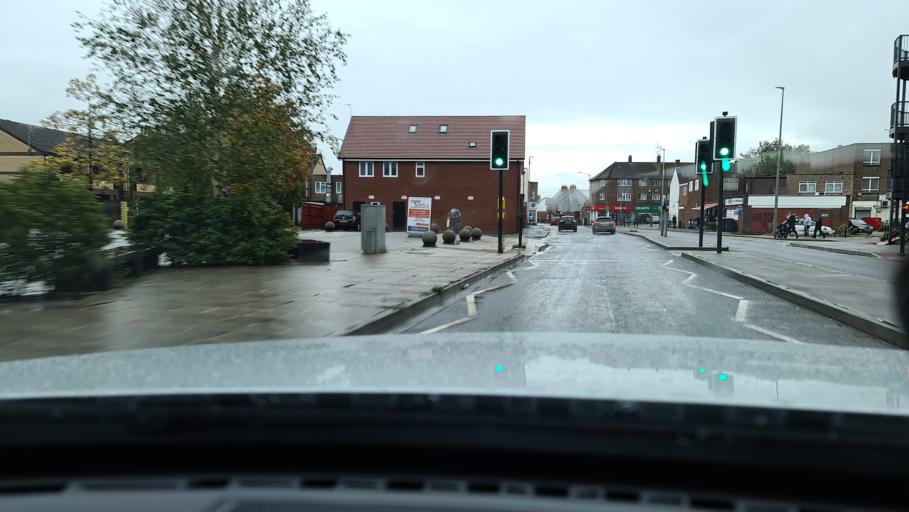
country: GB
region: England
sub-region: Buckinghamshire
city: Bletchley
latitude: 51.9963
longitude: -0.7276
